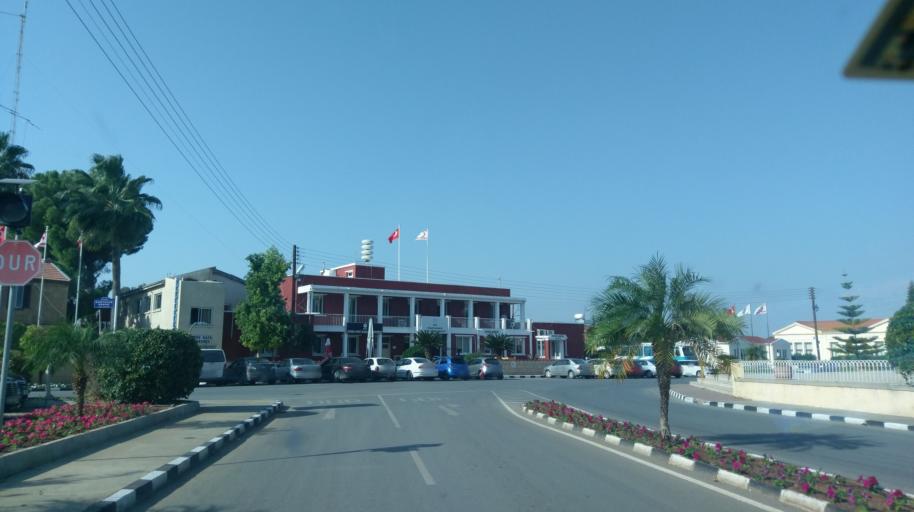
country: CY
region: Lefkosia
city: Morfou
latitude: 35.2006
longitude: 32.9898
